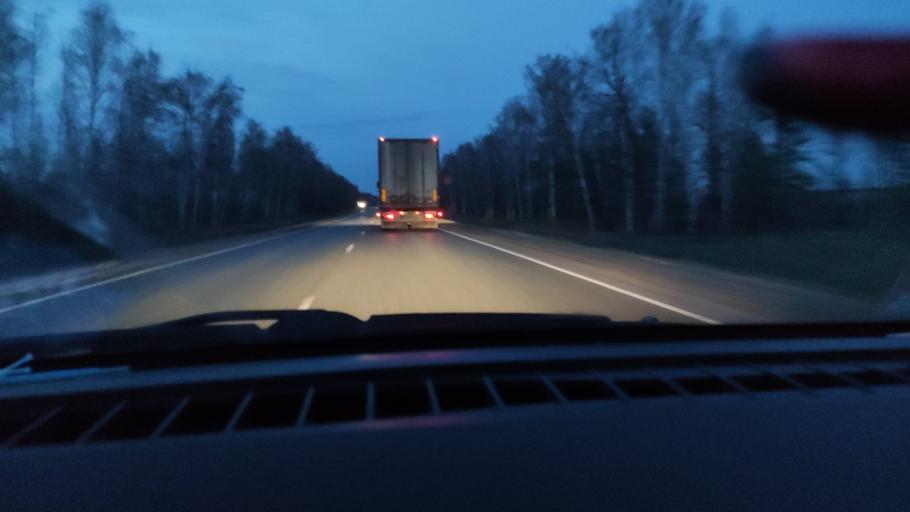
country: RU
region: Saratov
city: Sennoy
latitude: 52.1277
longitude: 46.8565
